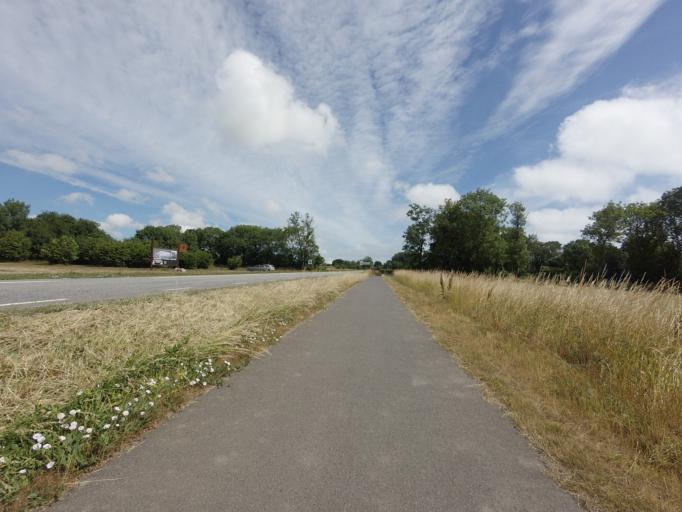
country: SE
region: Skane
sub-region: Simrishamns Kommun
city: Simrishamn
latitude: 55.4967
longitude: 14.3169
